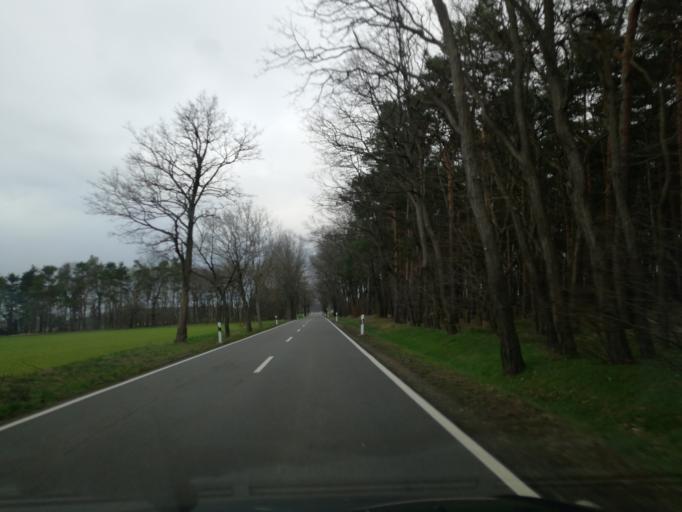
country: DE
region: Brandenburg
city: Vetschau
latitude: 51.7474
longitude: 14.0522
